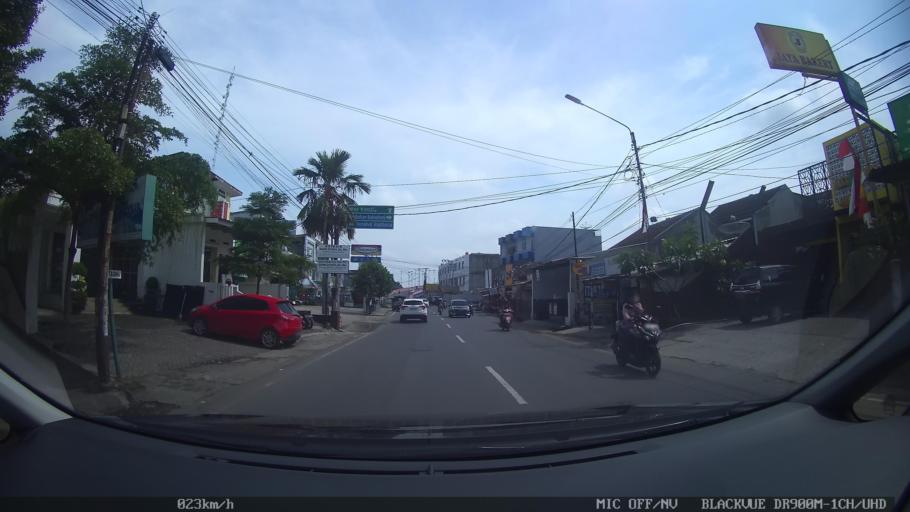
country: ID
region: Lampung
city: Kedaton
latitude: -5.3745
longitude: 105.2738
